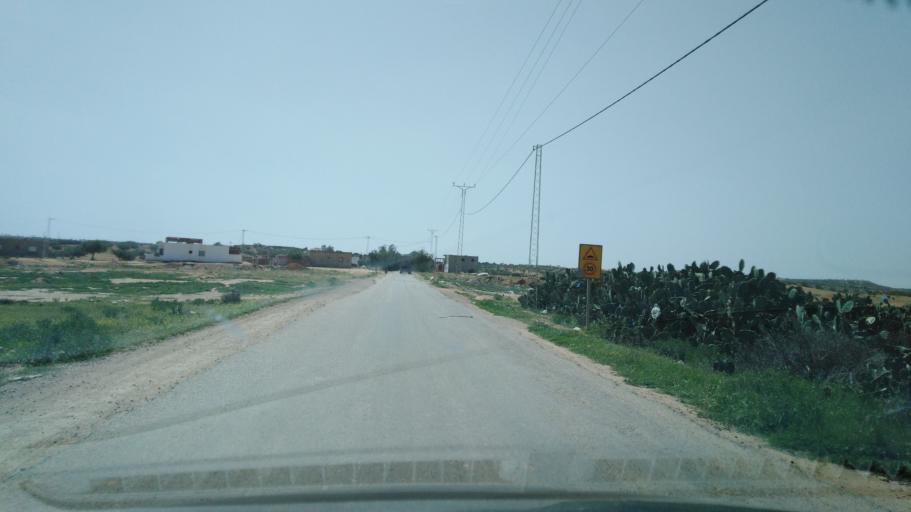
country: TN
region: Safaqis
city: Sfax
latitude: 34.7263
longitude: 10.5292
